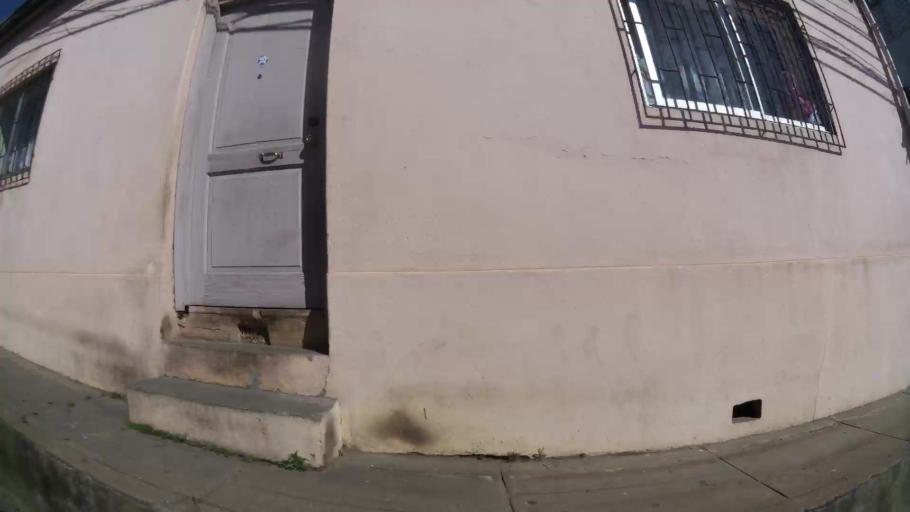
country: CL
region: Valparaiso
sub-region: Provincia de Valparaiso
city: Valparaiso
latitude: -33.0434
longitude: -71.6353
